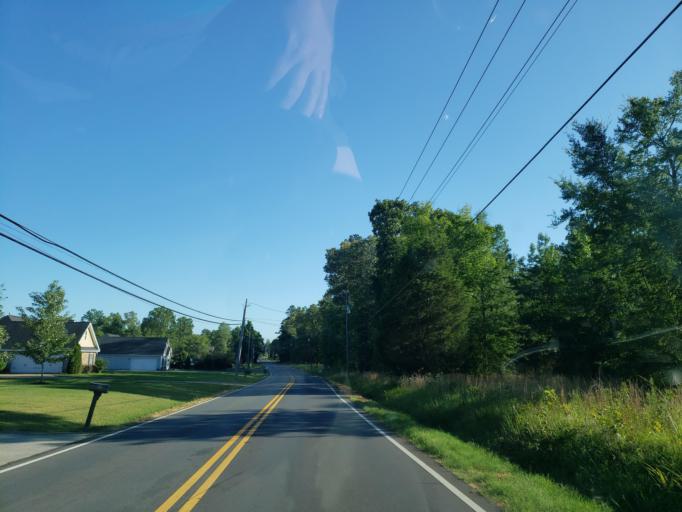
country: US
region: Georgia
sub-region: Floyd County
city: Rome
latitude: 34.3272
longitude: -85.1620
